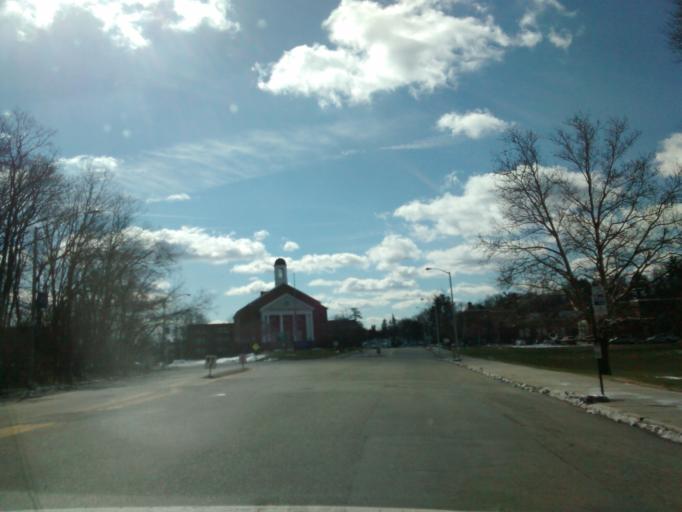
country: US
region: Massachusetts
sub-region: Worcester County
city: Worcester
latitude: 42.2686
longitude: -71.8412
